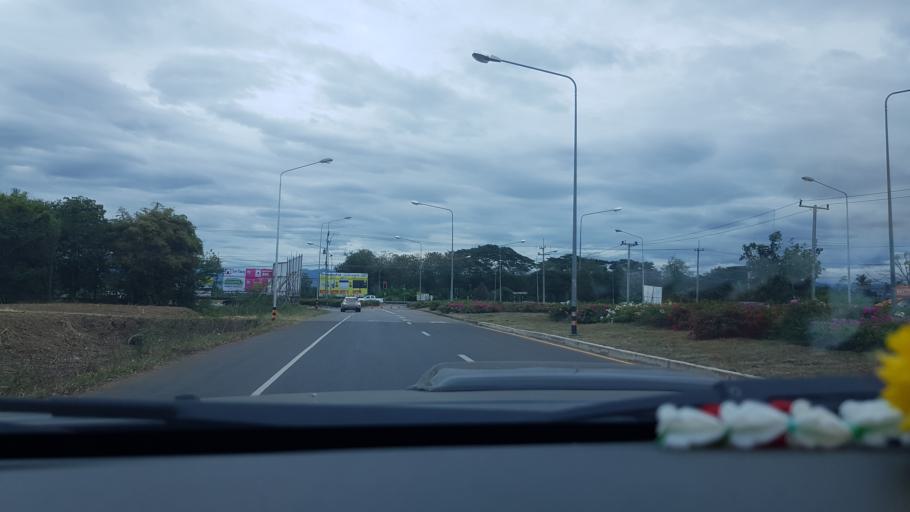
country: TH
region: Phetchabun
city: Phetchabun
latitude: 16.4974
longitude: 101.1565
